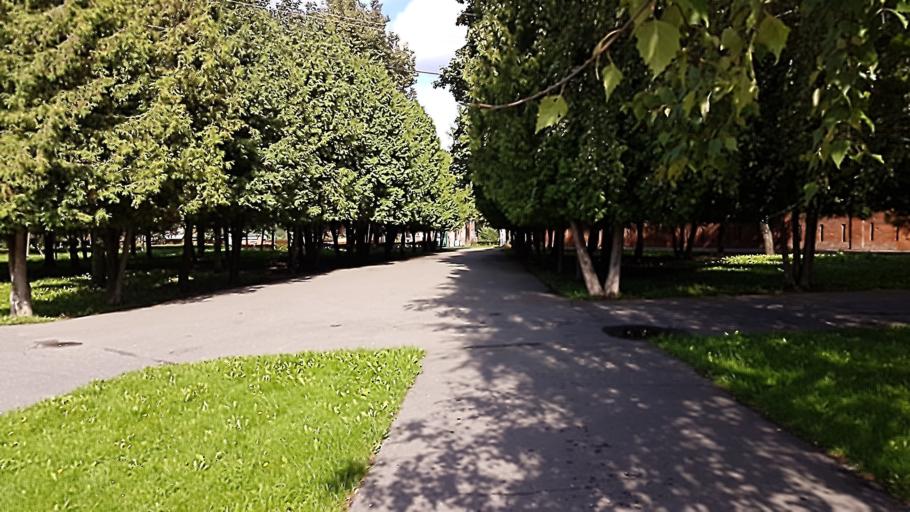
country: RU
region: Moskovskaya
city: Kolomna
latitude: 55.0949
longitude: 38.7704
